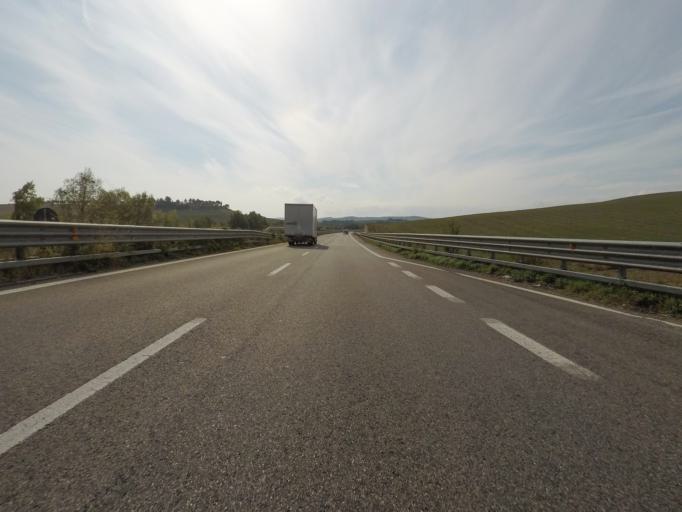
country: IT
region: Tuscany
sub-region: Provincia di Siena
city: Isola D'Arbia
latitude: 43.2632
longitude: 11.3288
